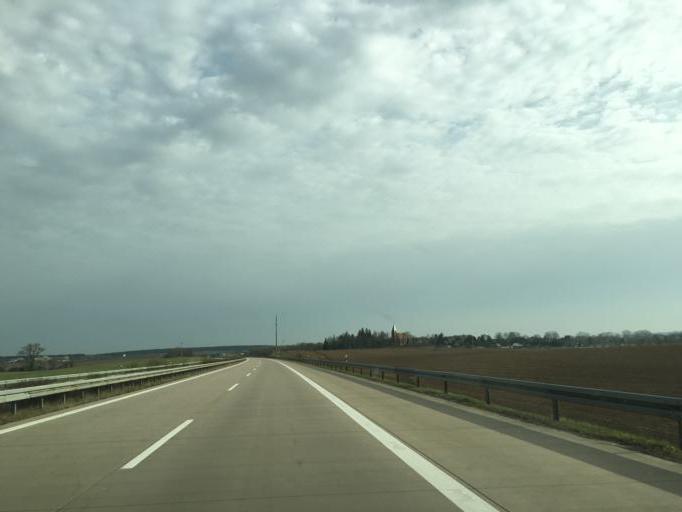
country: DE
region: Mecklenburg-Vorpommern
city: Krakow am See
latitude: 53.6022
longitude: 12.3681
